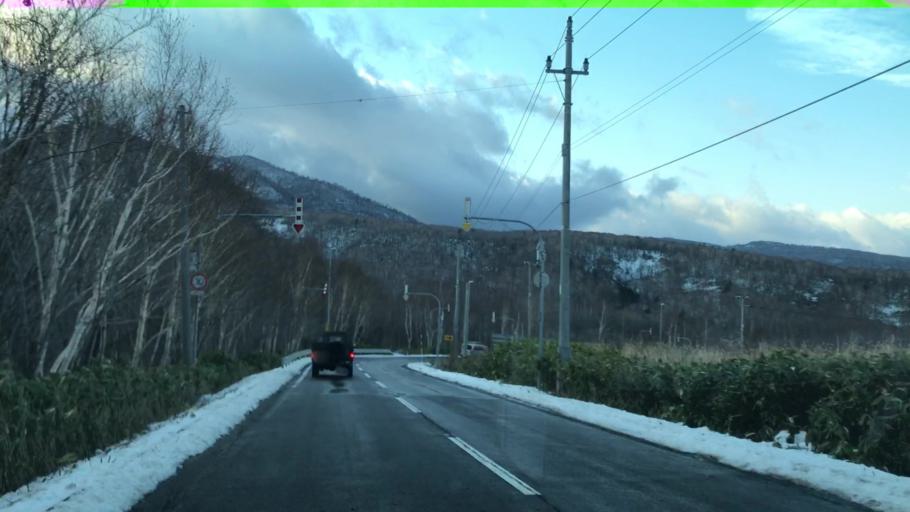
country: JP
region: Hokkaido
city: Otaru
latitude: 43.0887
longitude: 140.9739
